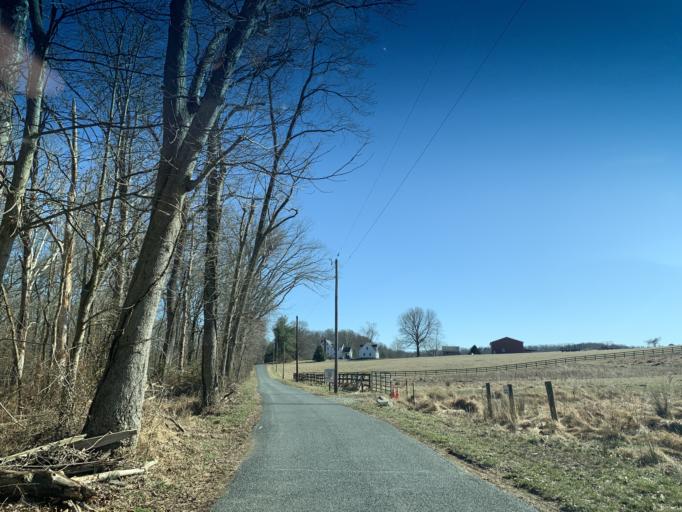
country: US
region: Maryland
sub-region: Harford County
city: Aberdeen
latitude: 39.6268
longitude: -76.2359
